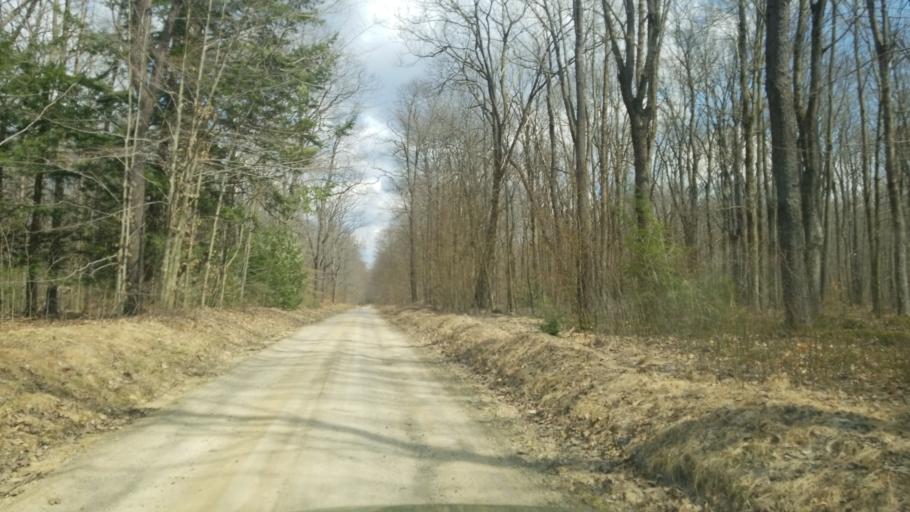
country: US
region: Pennsylvania
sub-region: Clearfield County
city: Clearfield
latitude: 41.1597
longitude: -78.5115
